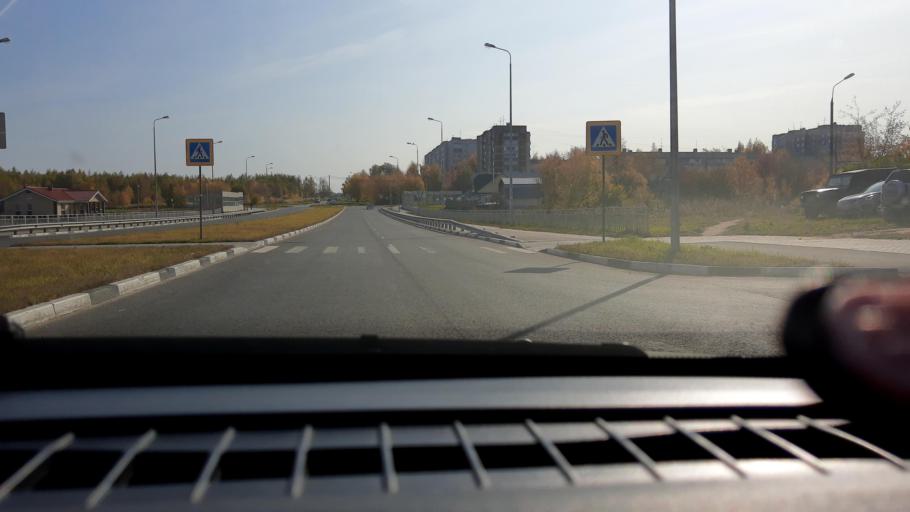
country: RU
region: Nizjnij Novgorod
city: Kstovo
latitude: 56.1545
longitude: 44.2159
